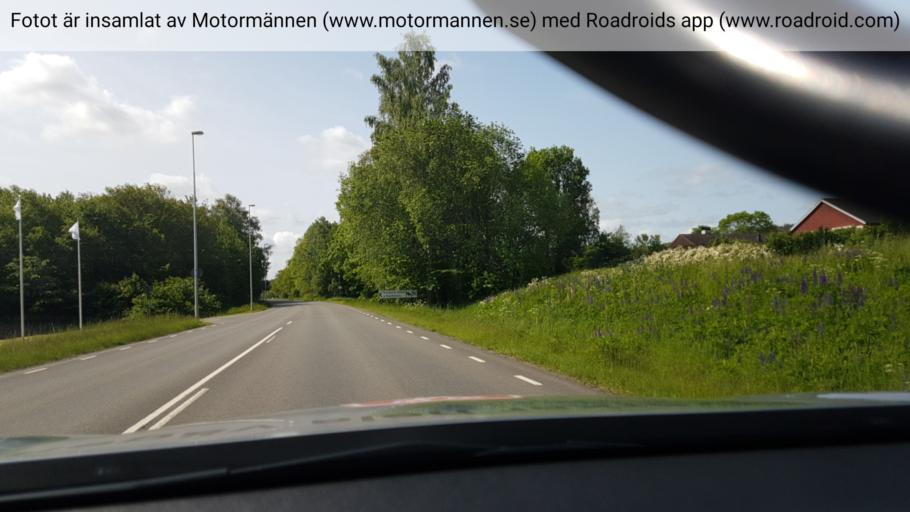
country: SE
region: Vaestra Goetaland
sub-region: Skovde Kommun
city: Skoevde
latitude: 58.4221
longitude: 13.8469
